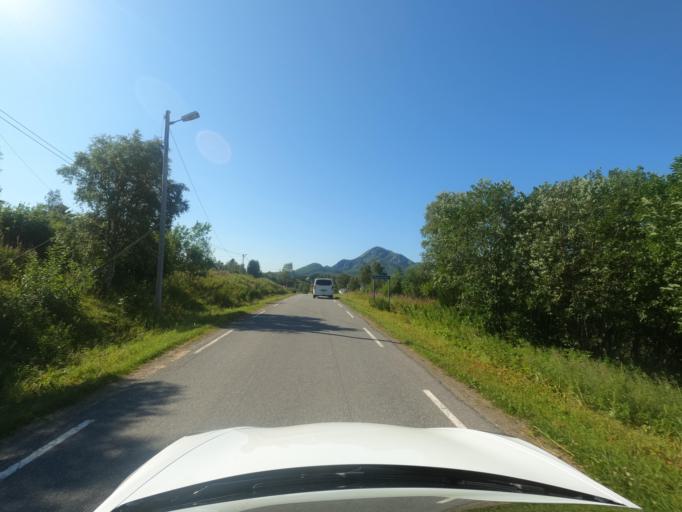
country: NO
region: Nordland
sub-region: Hadsel
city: Stokmarknes
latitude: 68.3163
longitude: 14.9929
